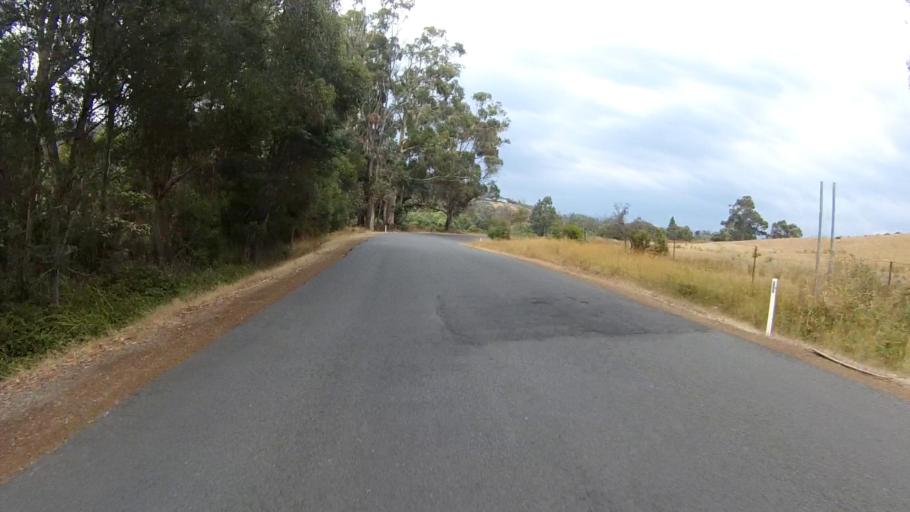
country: AU
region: Tasmania
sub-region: Huon Valley
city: Cygnet
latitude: -43.1821
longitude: 147.1121
